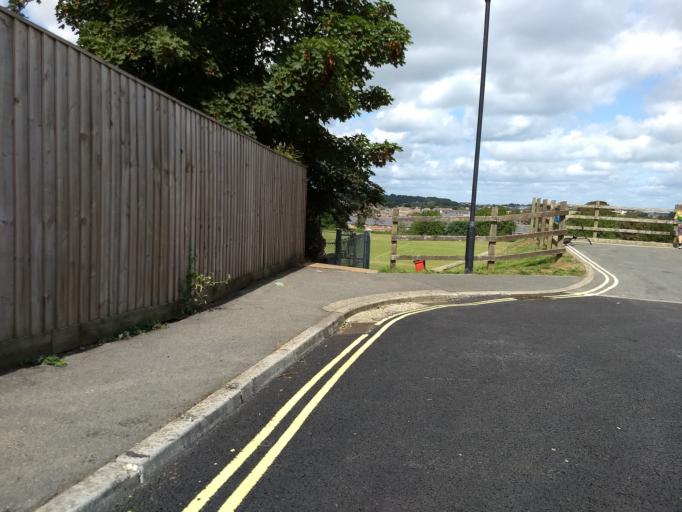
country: GB
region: England
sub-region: Isle of Wight
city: Newport
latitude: 50.6932
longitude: -1.2988
